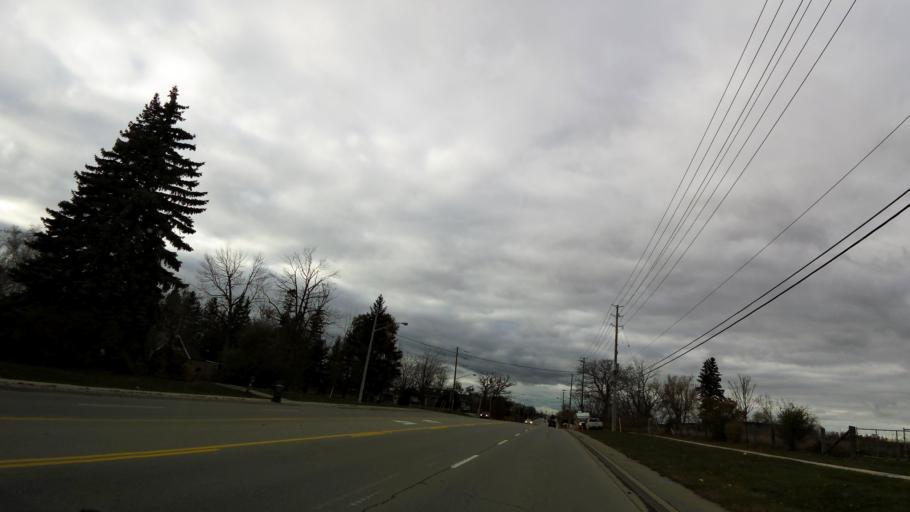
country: CA
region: Ontario
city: Brampton
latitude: 43.6692
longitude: -79.7131
